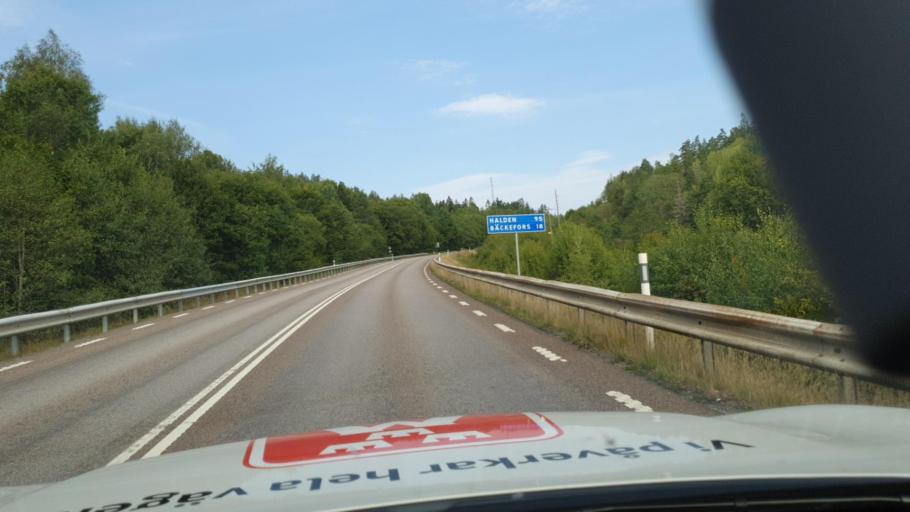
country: SE
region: Vaestra Goetaland
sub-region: Melleruds Kommun
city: Mellerud
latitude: 58.7292
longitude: 12.3608
